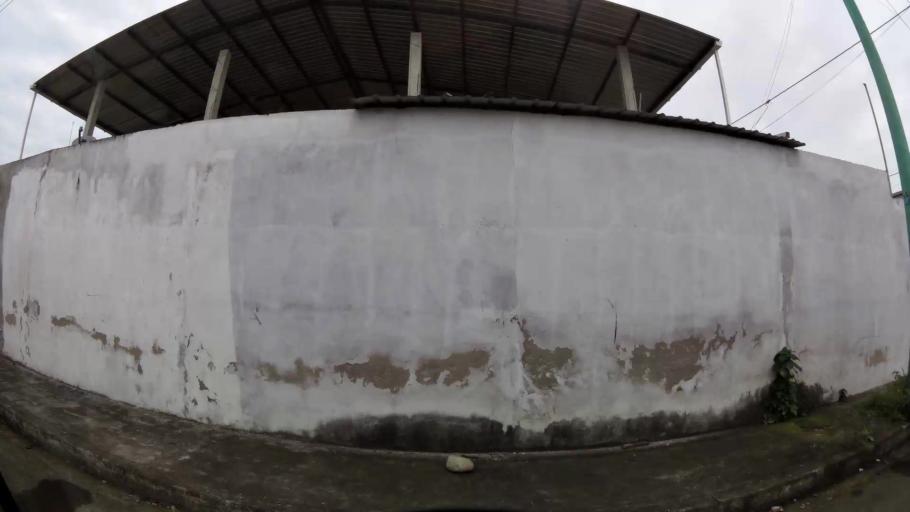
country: EC
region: El Oro
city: Machala
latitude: -3.2541
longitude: -79.9466
